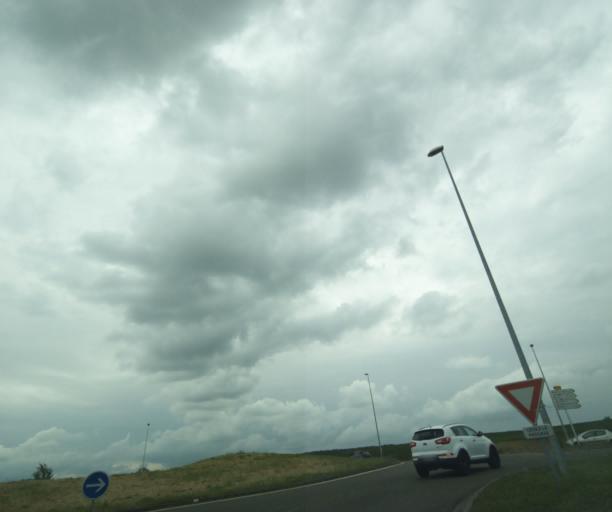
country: FR
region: Ile-de-France
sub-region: Departement des Yvelines
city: Ecquevilly
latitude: 48.9457
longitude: 1.9296
